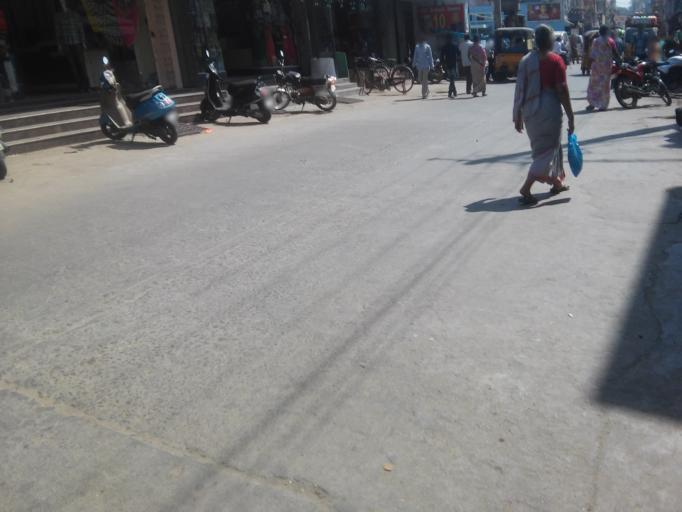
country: IN
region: Andhra Pradesh
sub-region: Chittoor
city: Chittoor
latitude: 13.2189
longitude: 79.0990
